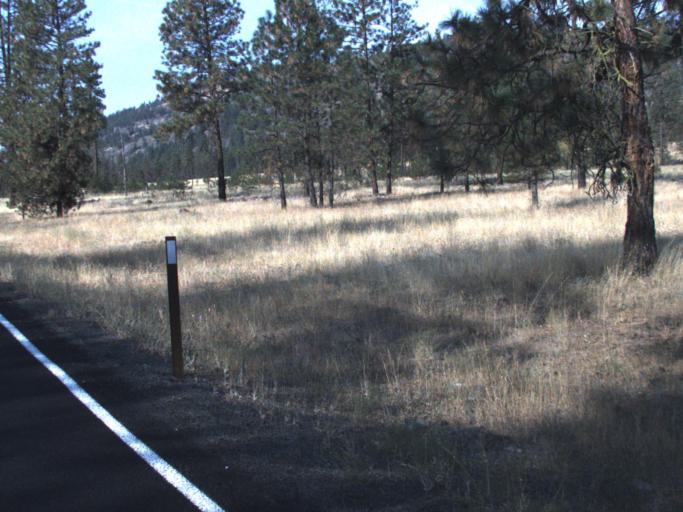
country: US
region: Washington
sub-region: Spokane County
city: Airway Heights
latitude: 47.8513
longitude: -117.7160
